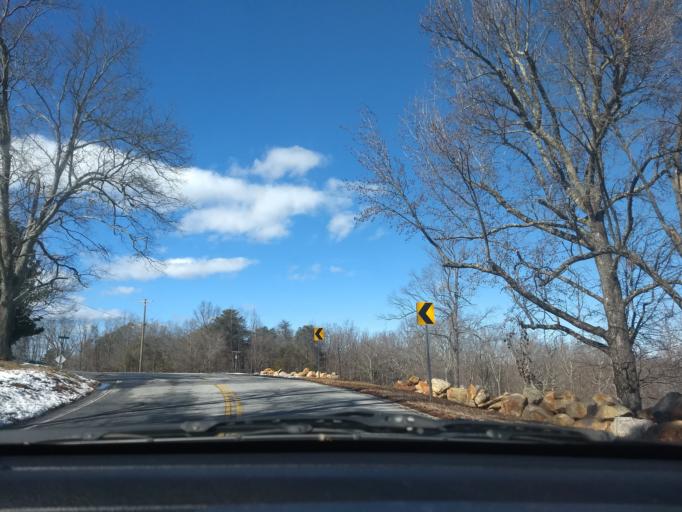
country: US
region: South Carolina
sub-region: Greenville County
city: Greenville
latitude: 34.8975
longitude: -82.3800
